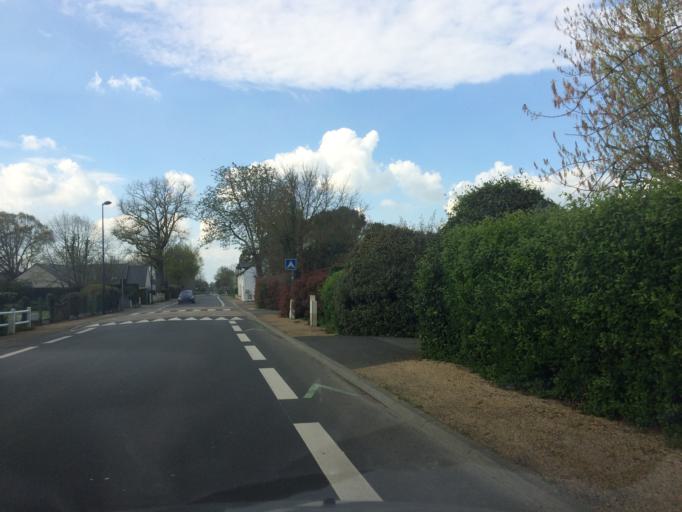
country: FR
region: Pays de la Loire
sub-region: Departement de la Loire-Atlantique
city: Heric
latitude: 47.4187
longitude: -1.6555
